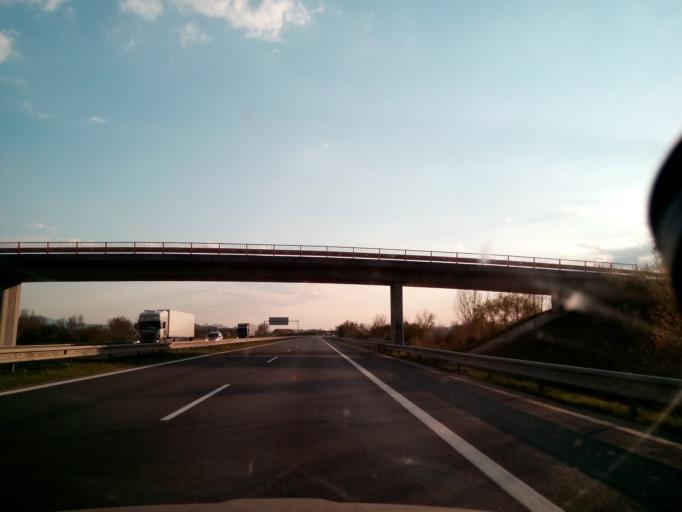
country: SK
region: Nitriansky
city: Ilava
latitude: 48.9915
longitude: 18.2059
